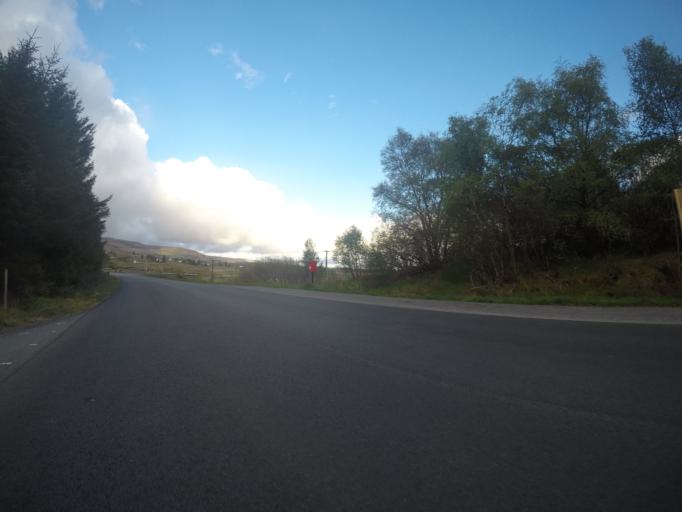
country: GB
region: Scotland
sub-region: Highland
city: Isle of Skye
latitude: 57.4516
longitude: -6.3042
